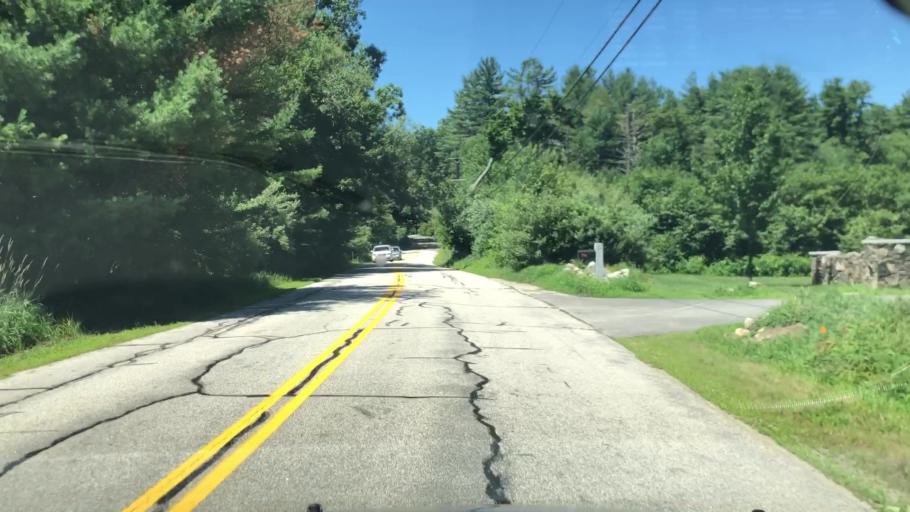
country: US
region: New Hampshire
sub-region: Hillsborough County
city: Milford
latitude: 42.8330
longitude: -71.5778
